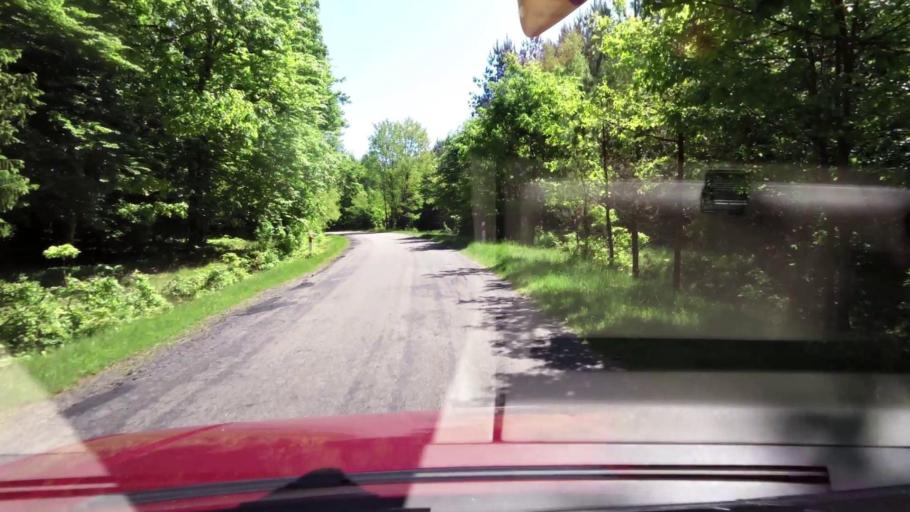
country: PL
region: West Pomeranian Voivodeship
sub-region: Powiat koszalinski
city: Bobolice
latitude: 54.0702
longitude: 16.5049
